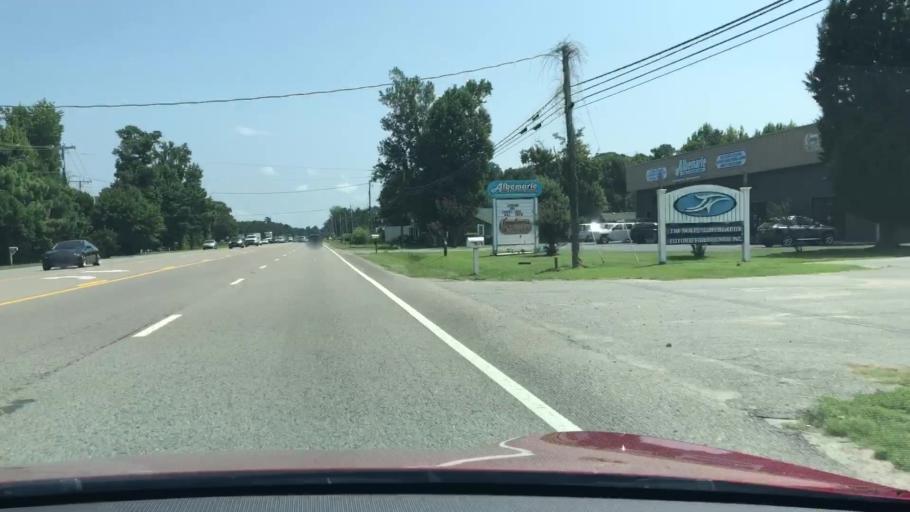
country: US
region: North Carolina
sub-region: Dare County
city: Southern Shores
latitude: 36.1088
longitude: -75.8232
